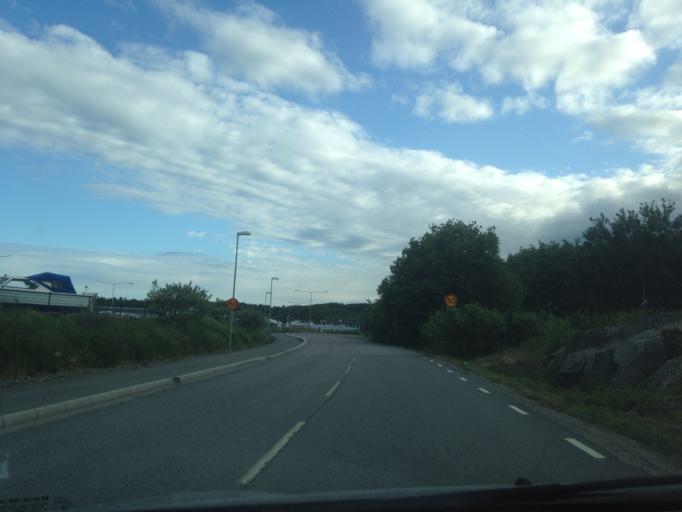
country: SE
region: Vaestra Goetaland
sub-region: Goteborg
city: Torslanda
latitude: 57.7622
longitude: 11.8088
